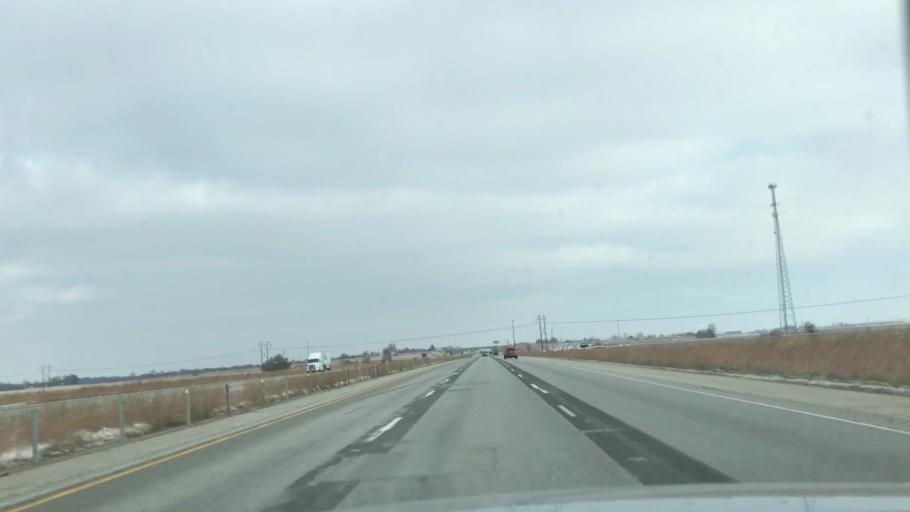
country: US
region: Illinois
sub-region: Sangamon County
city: Divernon
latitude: 39.6069
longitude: -89.6466
